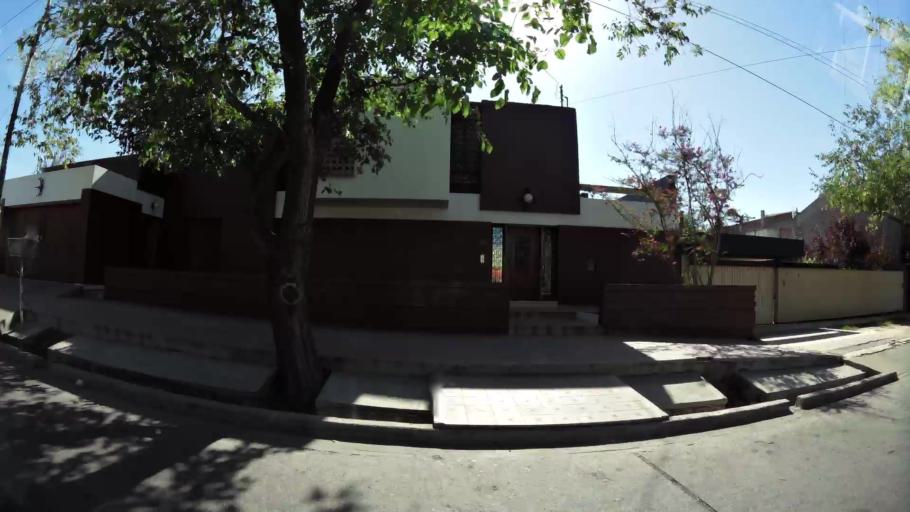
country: AR
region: Mendoza
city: Villa Nueva
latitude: -32.9054
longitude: -68.7897
